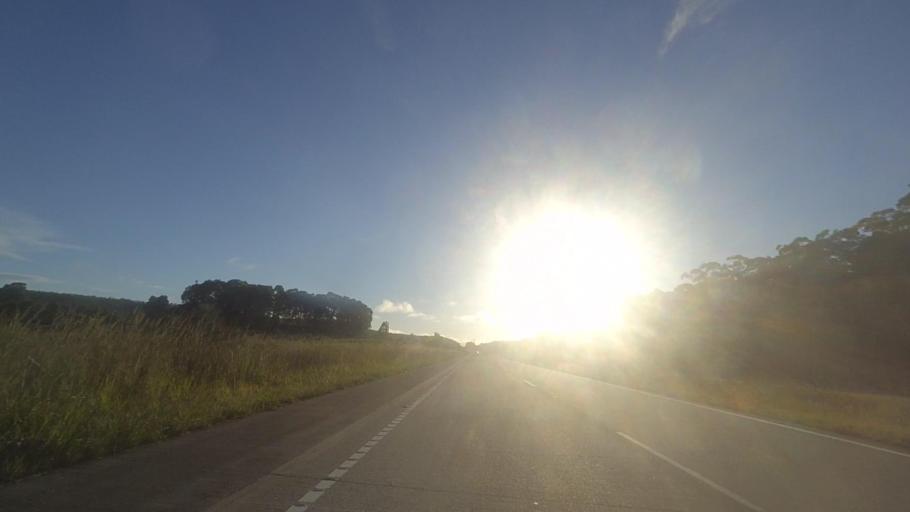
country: AU
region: New South Wales
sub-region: Great Lakes
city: Bulahdelah
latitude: -32.5260
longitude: 152.1953
